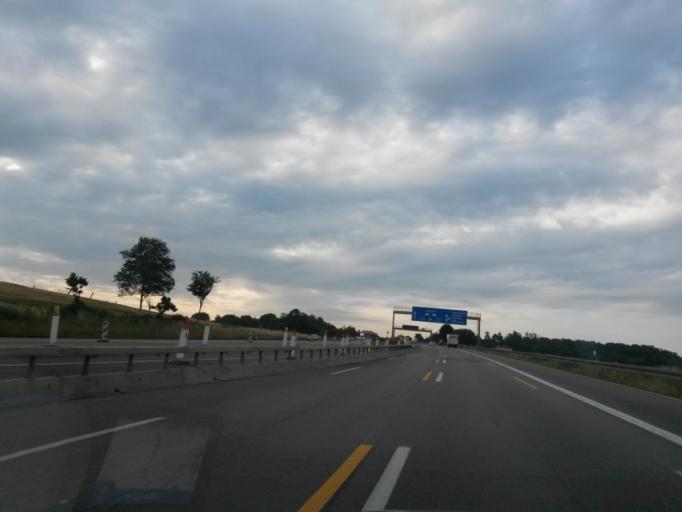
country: DE
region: Bavaria
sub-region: Upper Bavaria
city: Rohrbach
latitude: 48.5863
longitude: 11.5742
